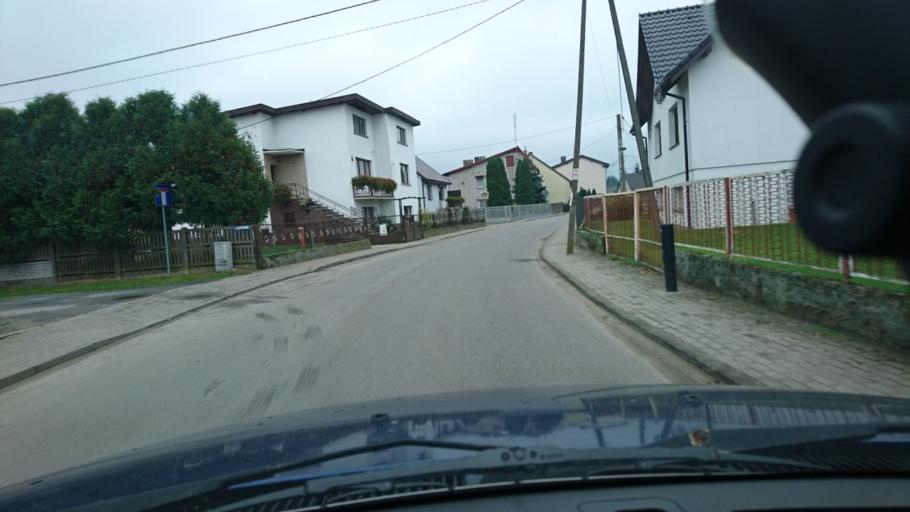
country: PL
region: Greater Poland Voivodeship
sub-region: Powiat krotoszynski
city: Sulmierzyce
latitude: 51.5681
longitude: 17.5891
